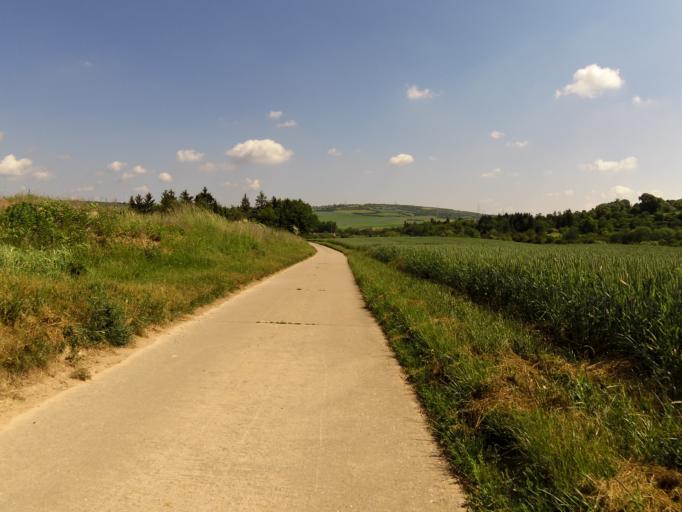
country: DE
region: Rheinland-Pfalz
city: Ebertsheim
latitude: 49.5605
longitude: 8.1072
